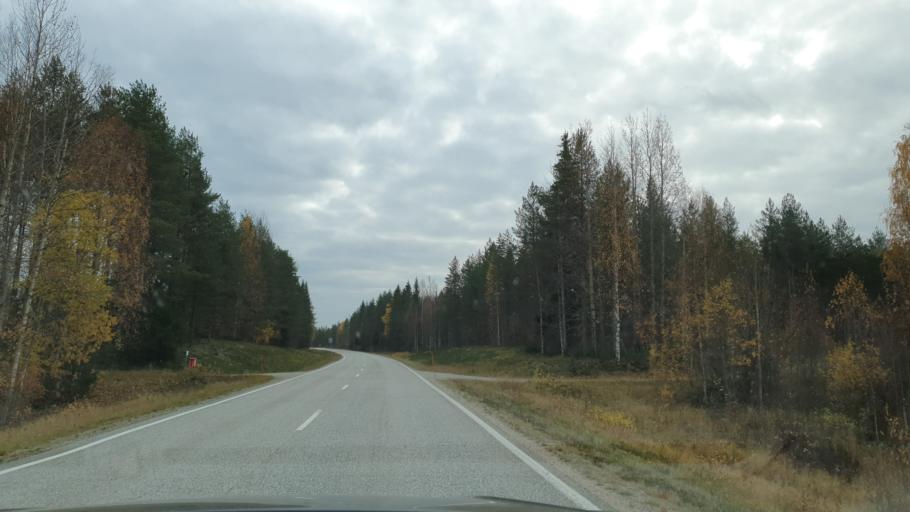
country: FI
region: Kainuu
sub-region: Kehys-Kainuu
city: Puolanka
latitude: 65.2432
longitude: 27.5815
